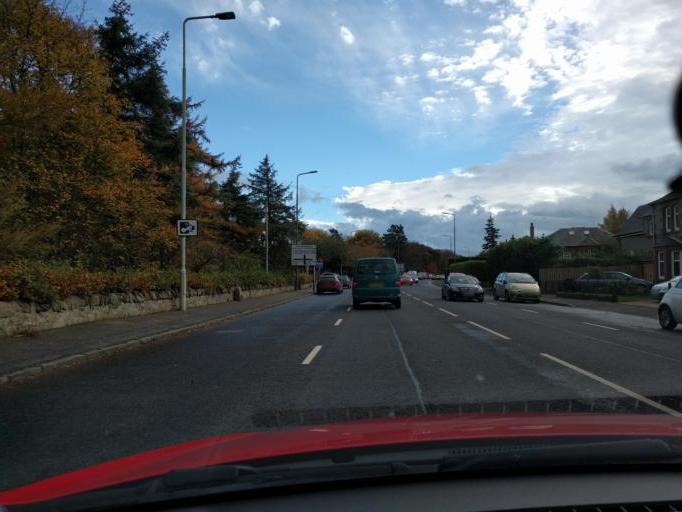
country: GB
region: Scotland
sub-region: Edinburgh
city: Edinburgh
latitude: 55.9033
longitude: -3.2060
